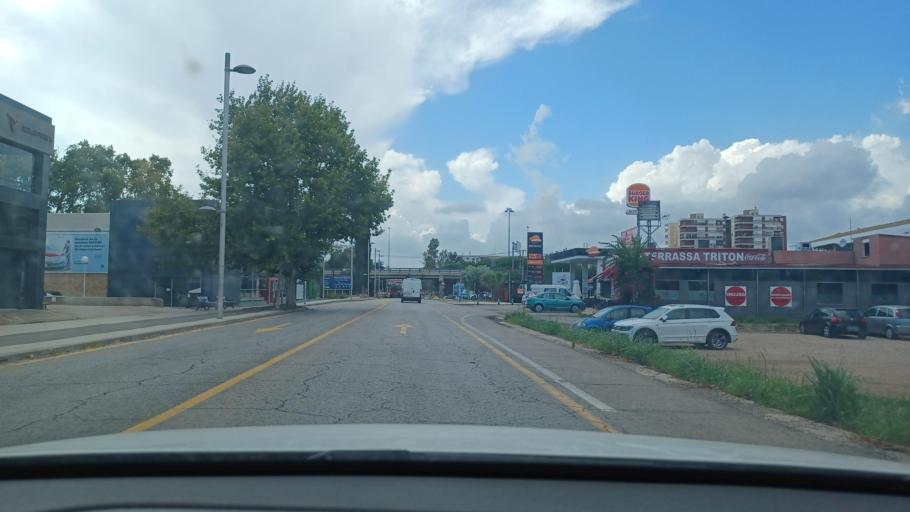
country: ES
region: Catalonia
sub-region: Provincia de Tarragona
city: Tarragona
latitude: 41.1165
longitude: 1.2295
